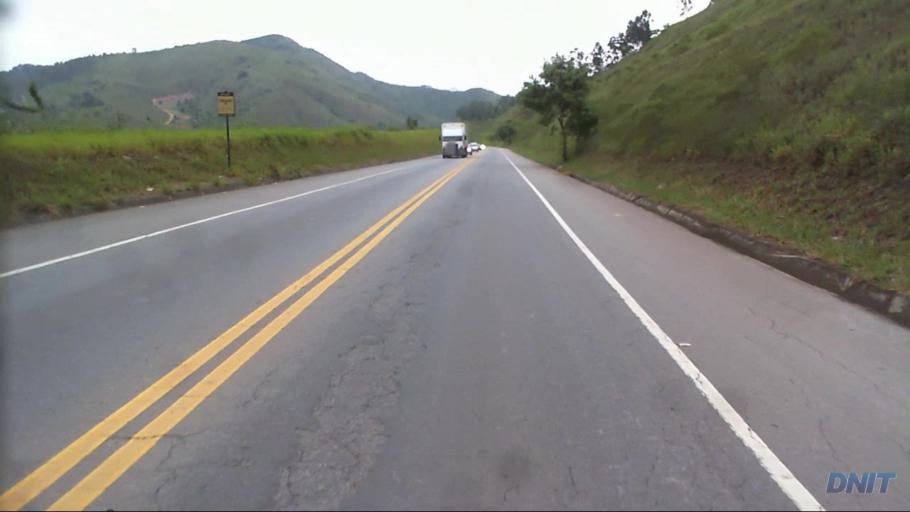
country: BR
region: Minas Gerais
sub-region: Coronel Fabriciano
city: Coronel Fabriciano
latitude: -19.5308
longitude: -42.5816
